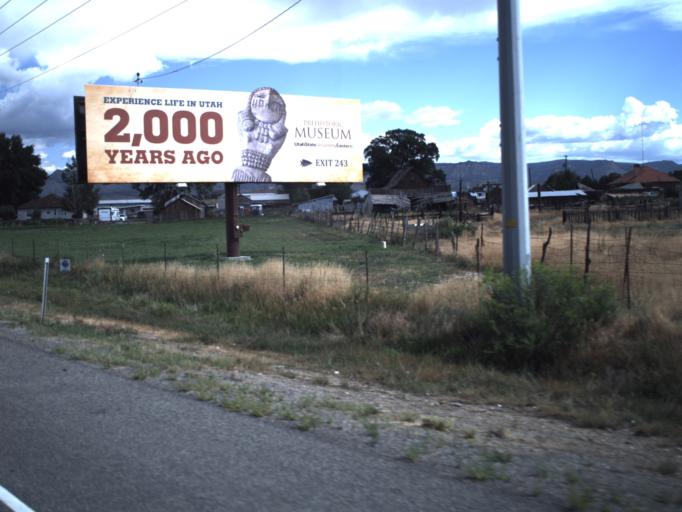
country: US
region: Utah
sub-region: Carbon County
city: Price
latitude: 39.5735
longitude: -110.7832
